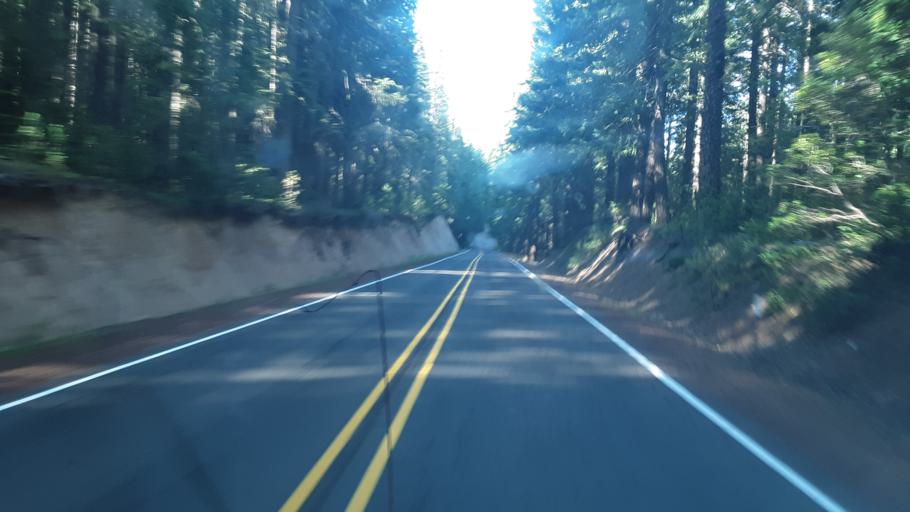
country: US
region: Oregon
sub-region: Jackson County
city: Shady Cove
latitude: 42.9397
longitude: -122.4192
